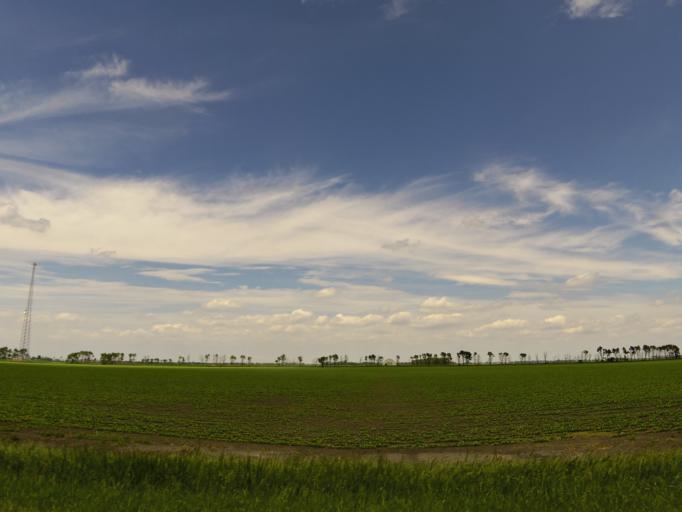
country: US
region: North Dakota
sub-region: Walsh County
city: Grafton
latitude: 48.2954
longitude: -97.2288
